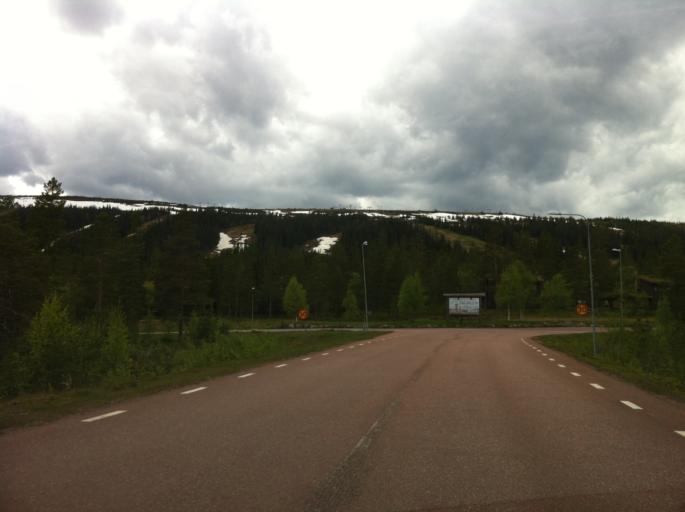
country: SE
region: Dalarna
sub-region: Malung-Saelens kommun
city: Malung
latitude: 61.1487
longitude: 13.2668
